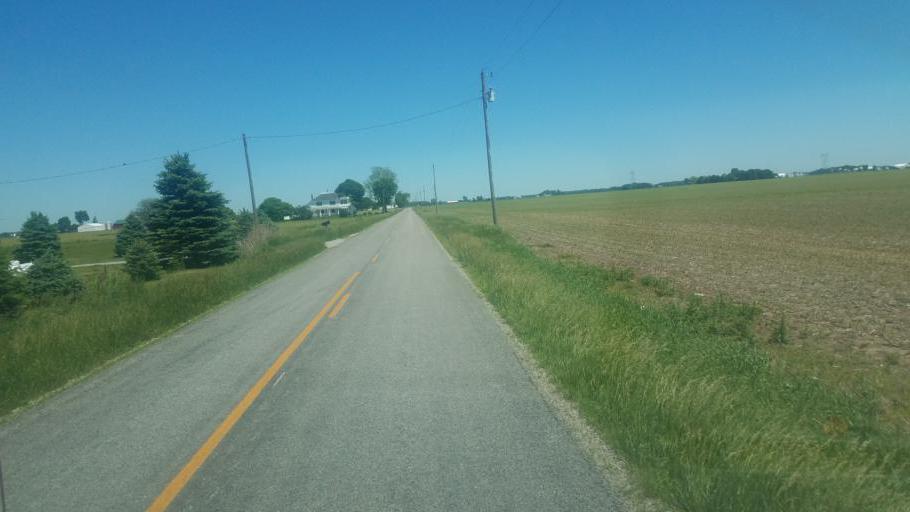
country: US
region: Ohio
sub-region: Shelby County
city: Sidney
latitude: 40.2103
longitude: -84.1046
